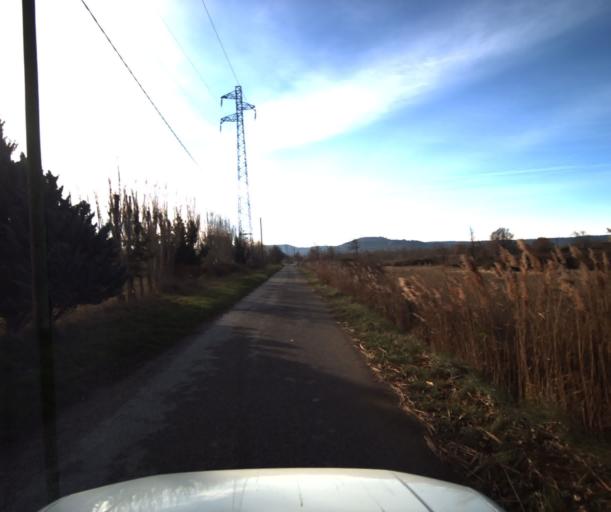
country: FR
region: Provence-Alpes-Cote d'Azur
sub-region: Departement du Vaucluse
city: Pertuis
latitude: 43.6835
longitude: 5.4712
